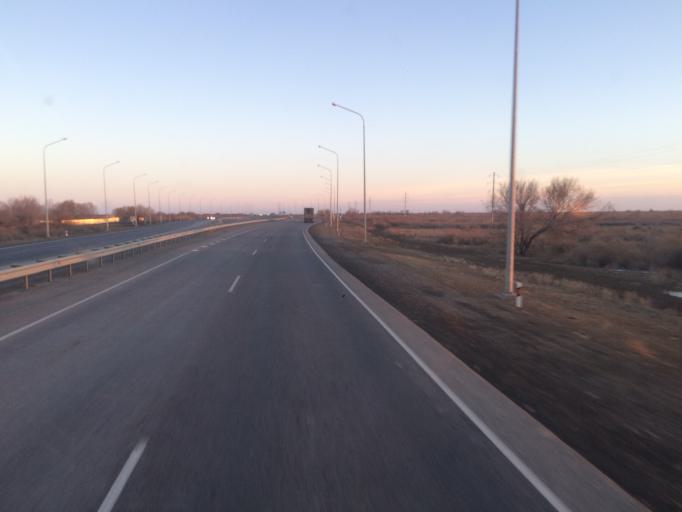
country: KZ
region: Qyzylorda
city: Shieli
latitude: 44.1332
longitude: 66.9759
